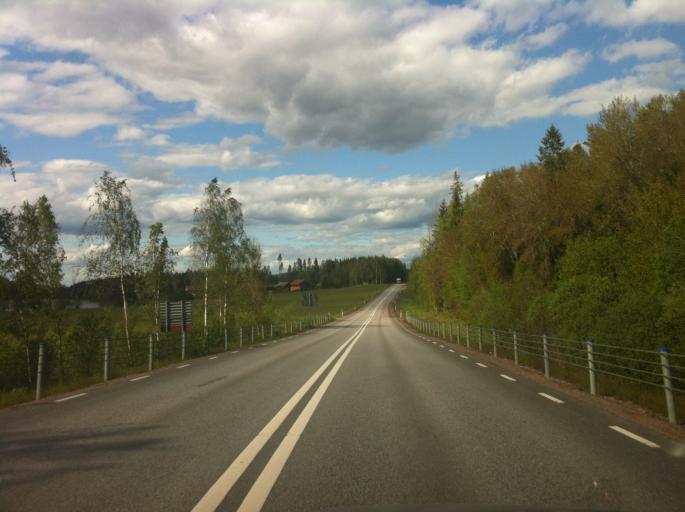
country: SE
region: Vaermland
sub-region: Storfors Kommun
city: Storfors
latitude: 59.4478
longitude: 14.2391
